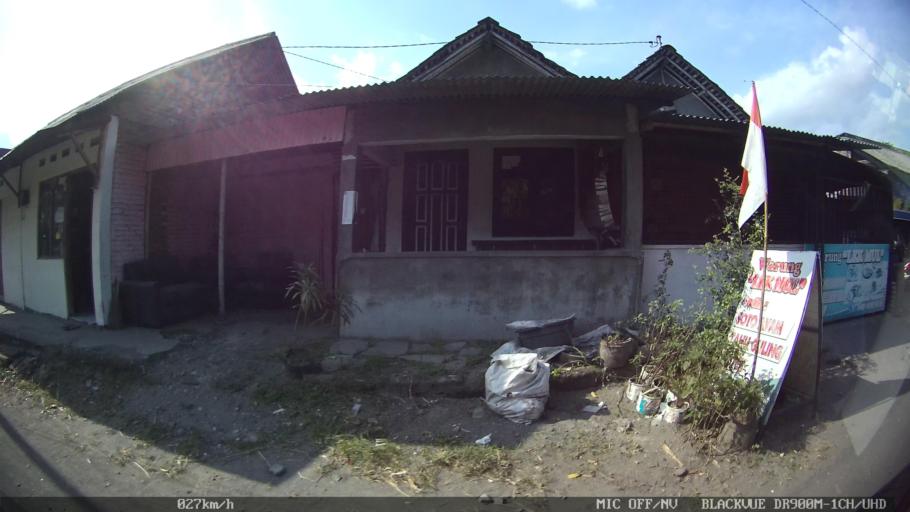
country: ID
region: Daerah Istimewa Yogyakarta
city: Kasihan
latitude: -7.8462
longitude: 110.3402
